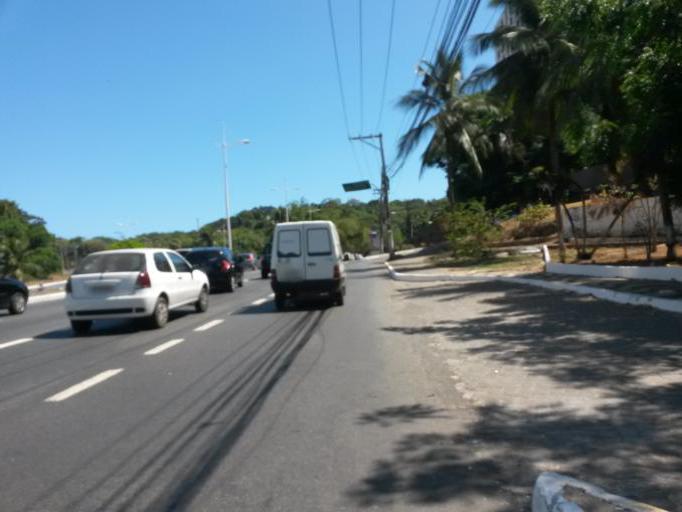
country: BR
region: Bahia
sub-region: Salvador
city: Salvador
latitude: -12.9933
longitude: -38.4759
